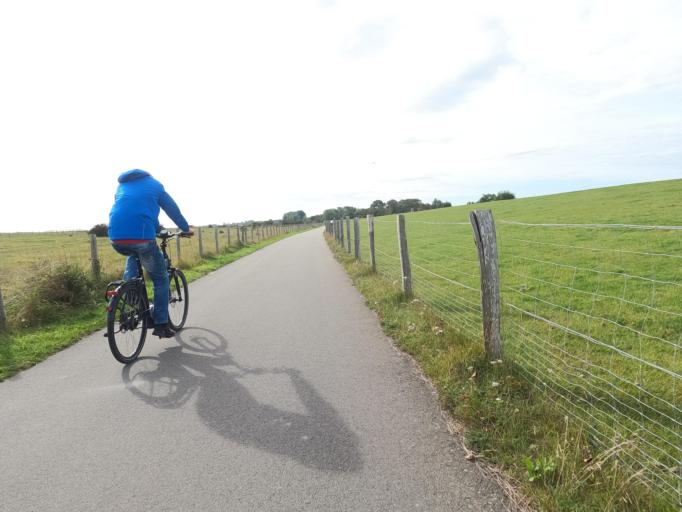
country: DE
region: Schleswig-Holstein
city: Dahme
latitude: 54.2584
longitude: 11.0811
